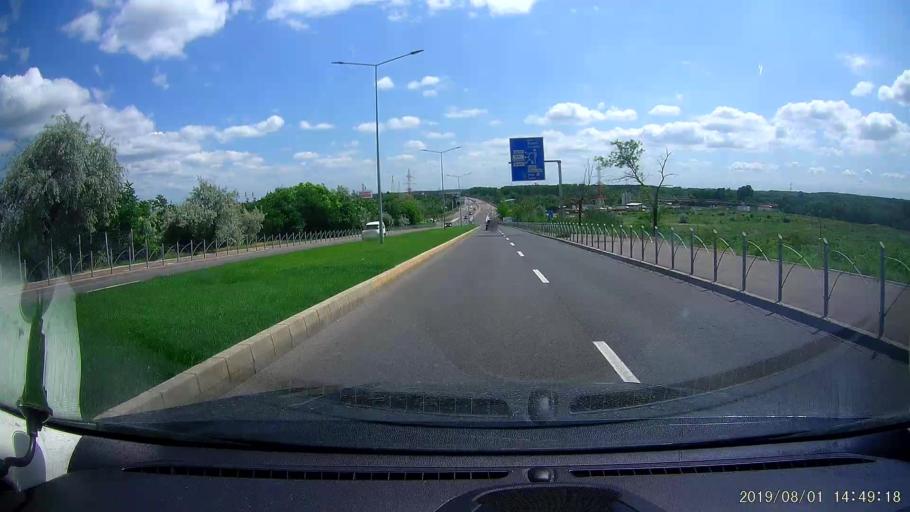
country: RO
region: Galati
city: Galati
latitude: 45.4068
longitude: 28.0151
